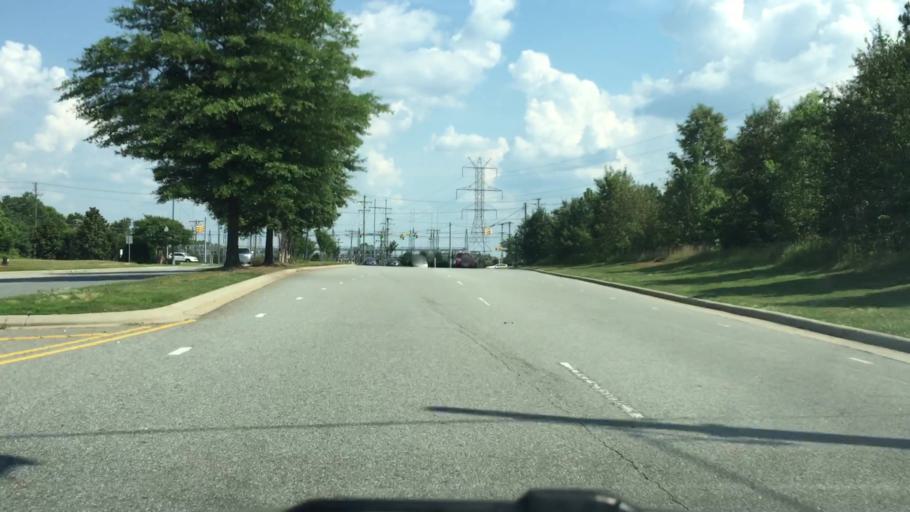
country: US
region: North Carolina
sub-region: Iredell County
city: Mooresville
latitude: 35.5822
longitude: -80.8814
